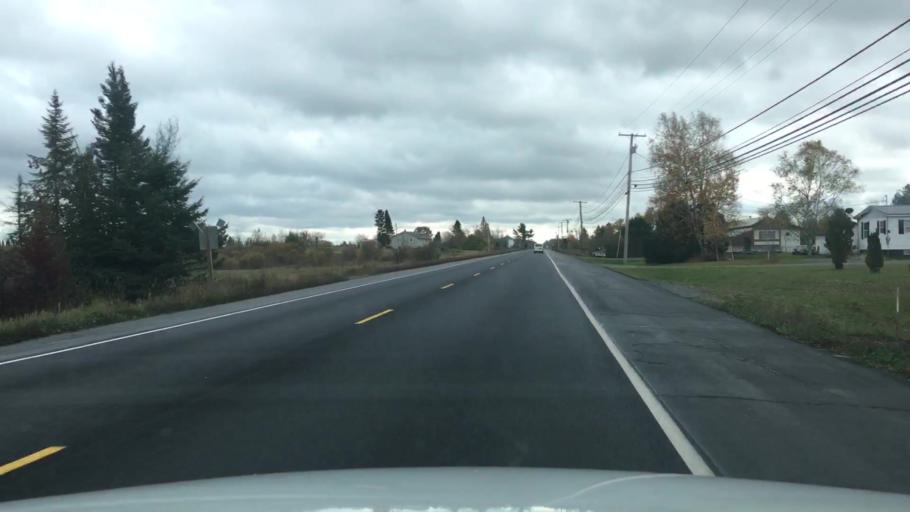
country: US
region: Maine
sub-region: Aroostook County
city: Houlton
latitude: 46.2538
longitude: -67.8408
